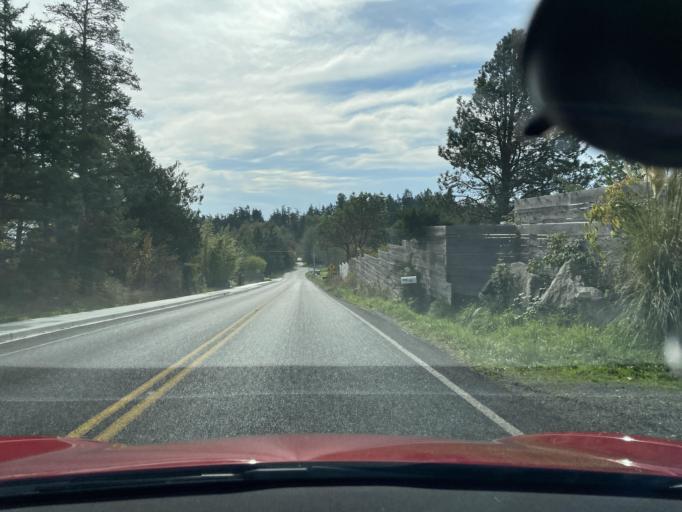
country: US
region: Washington
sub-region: San Juan County
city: Friday Harbor
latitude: 48.5241
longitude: -123.0177
